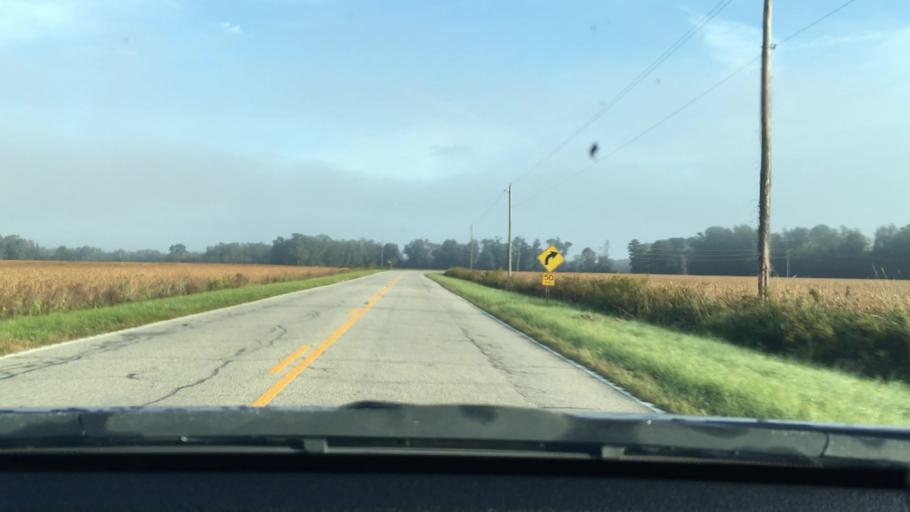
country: US
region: South Carolina
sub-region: Sumter County
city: East Sumter
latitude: 33.9851
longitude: -80.2969
